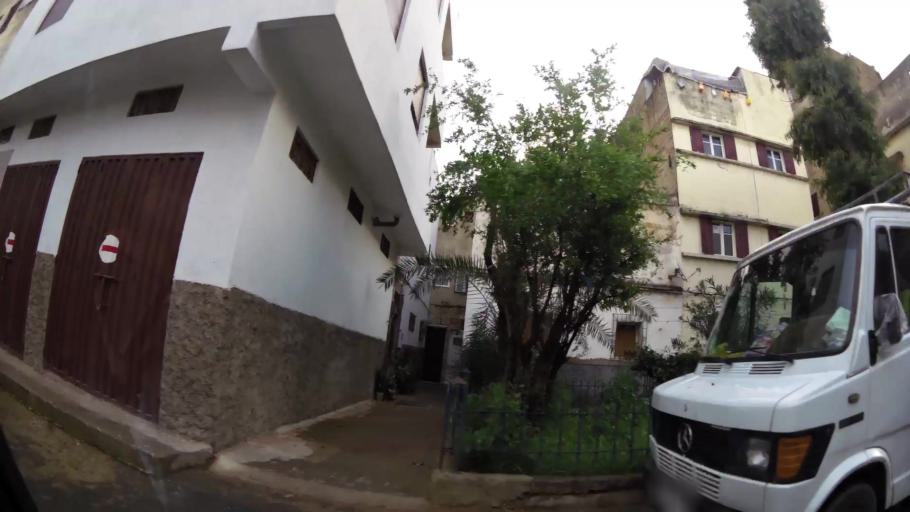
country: MA
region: Grand Casablanca
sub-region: Casablanca
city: Casablanca
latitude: 33.5481
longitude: -7.5768
